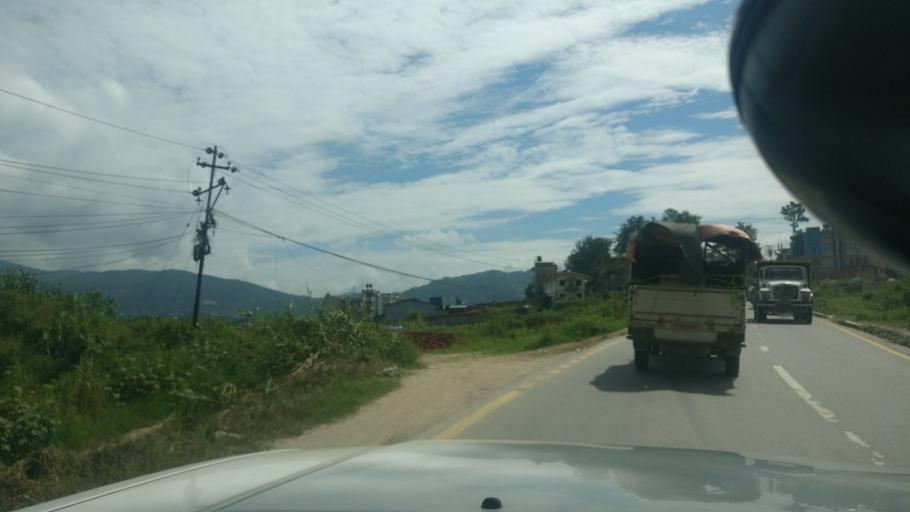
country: NP
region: Central Region
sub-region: Bagmati Zone
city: Bhaktapur
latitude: 27.6607
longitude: 85.4481
